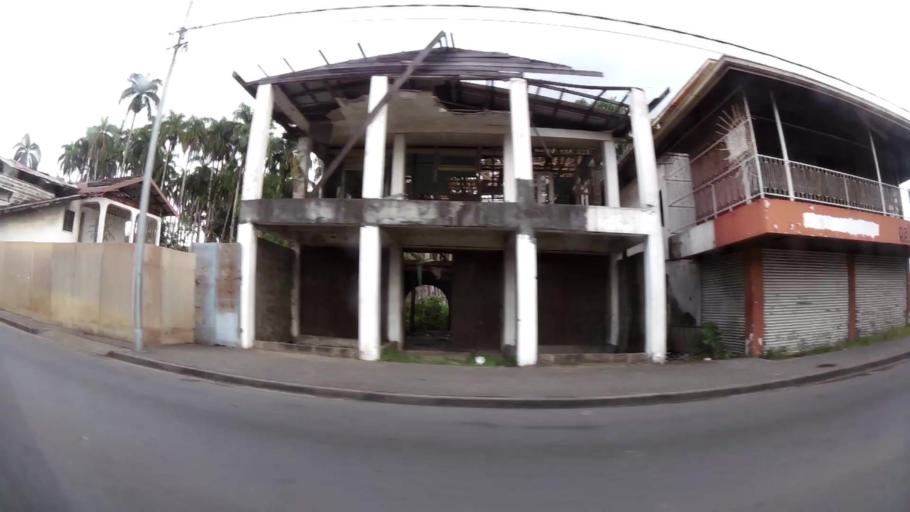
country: SR
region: Paramaribo
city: Paramaribo
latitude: 5.8272
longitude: -55.1492
